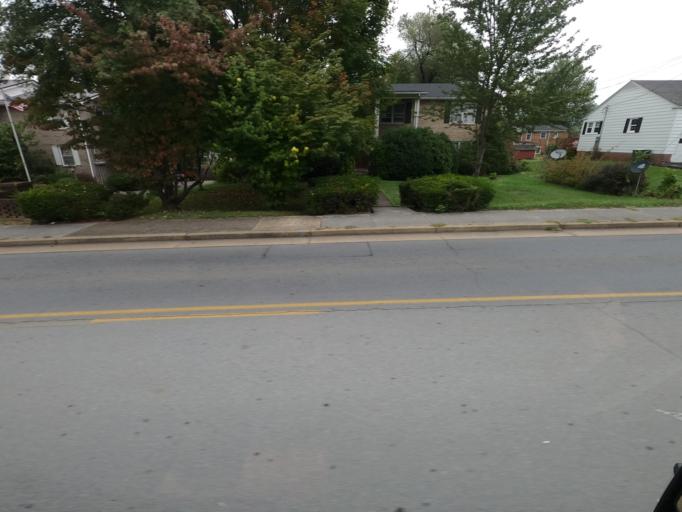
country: US
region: Tennessee
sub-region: Carter County
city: Elizabethton
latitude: 36.3456
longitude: -82.2255
